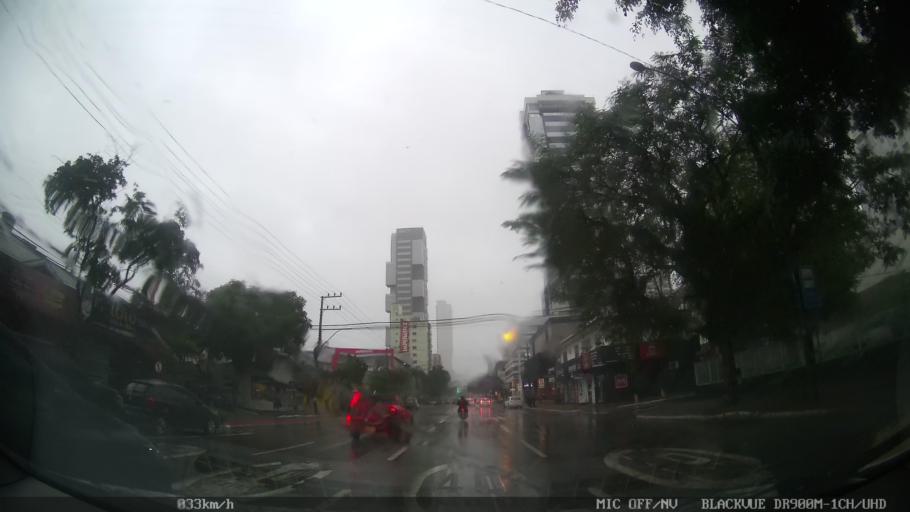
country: BR
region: Santa Catarina
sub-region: Balneario Camboriu
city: Balneario Camboriu
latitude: -26.9945
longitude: -48.6357
